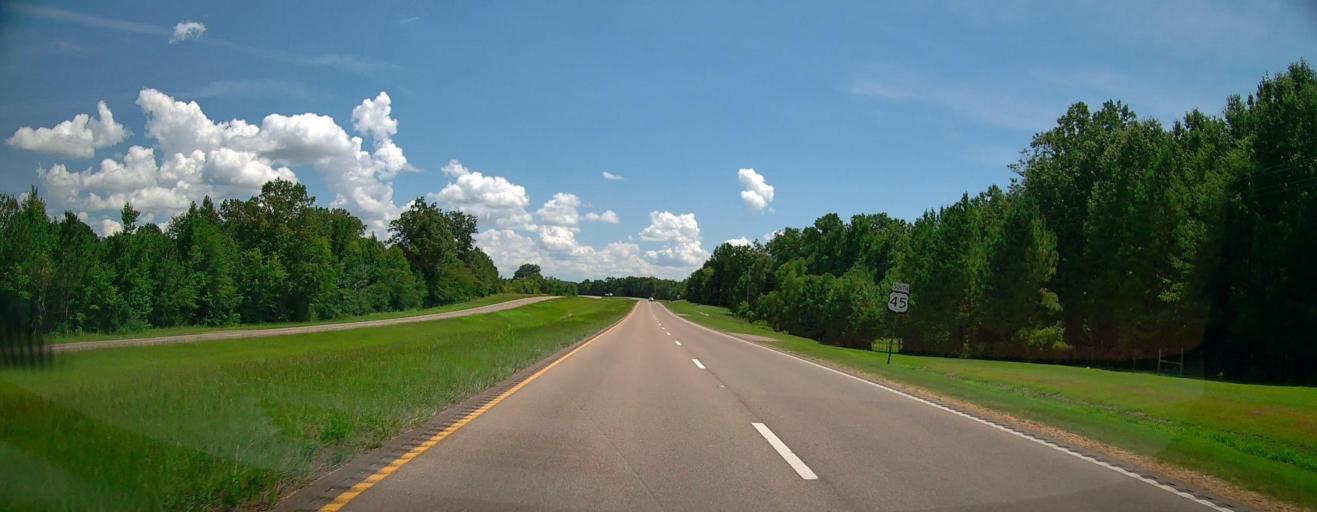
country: US
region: Mississippi
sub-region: Lee County
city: Nettleton
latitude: 33.9707
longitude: -88.6139
